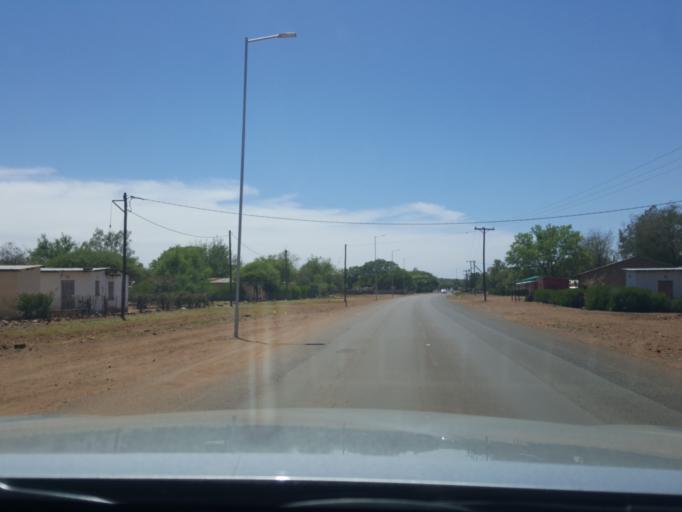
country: BW
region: South East
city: Ramotswa
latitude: -24.8660
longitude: 25.8653
